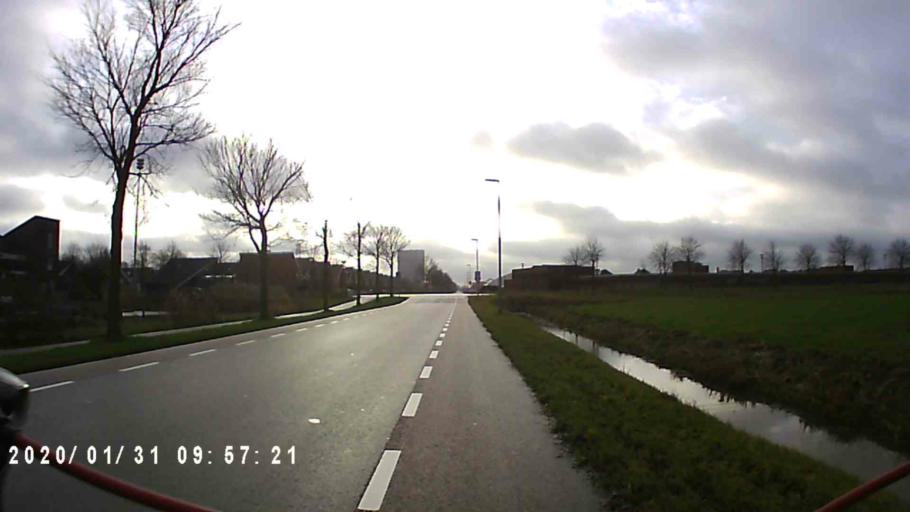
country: NL
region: Groningen
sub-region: Gemeente Groningen
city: Korrewegwijk
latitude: 53.2429
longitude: 6.5208
